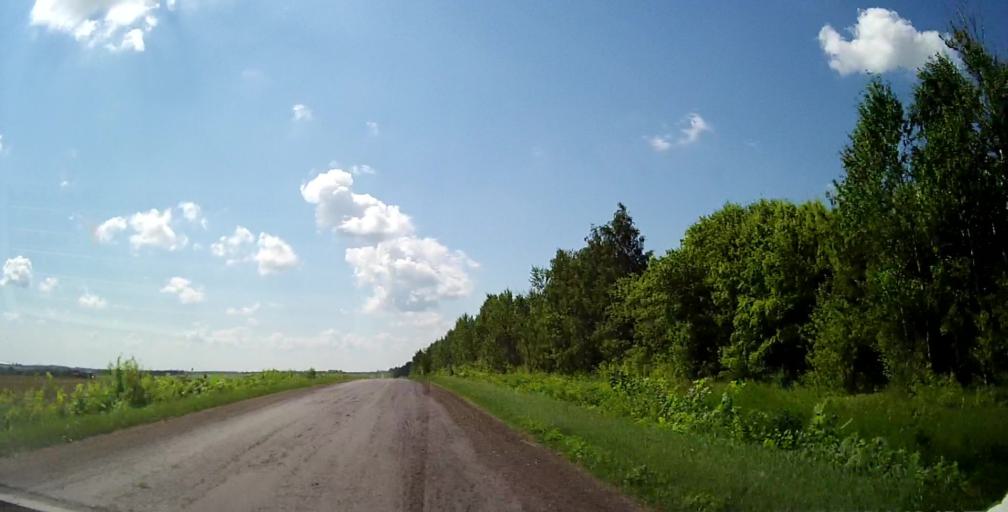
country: RU
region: Lipetsk
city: Chaplygin
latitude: 53.2920
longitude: 39.9575
